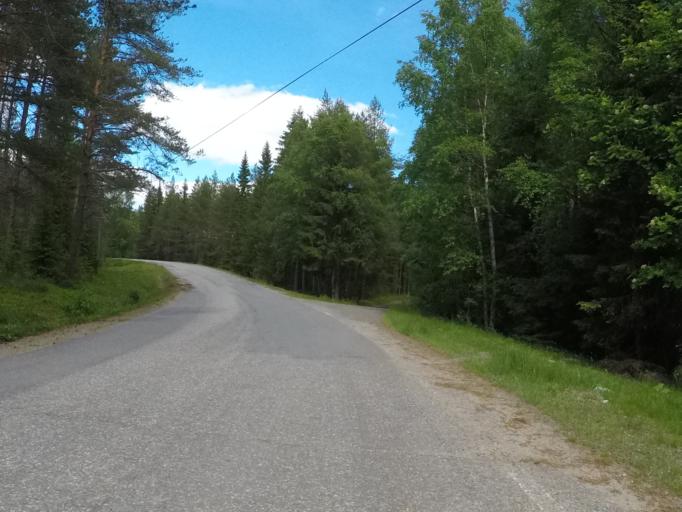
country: SE
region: Vaesterbotten
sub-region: Robertsfors Kommun
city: Robertsfors
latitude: 64.1750
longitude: 20.9615
